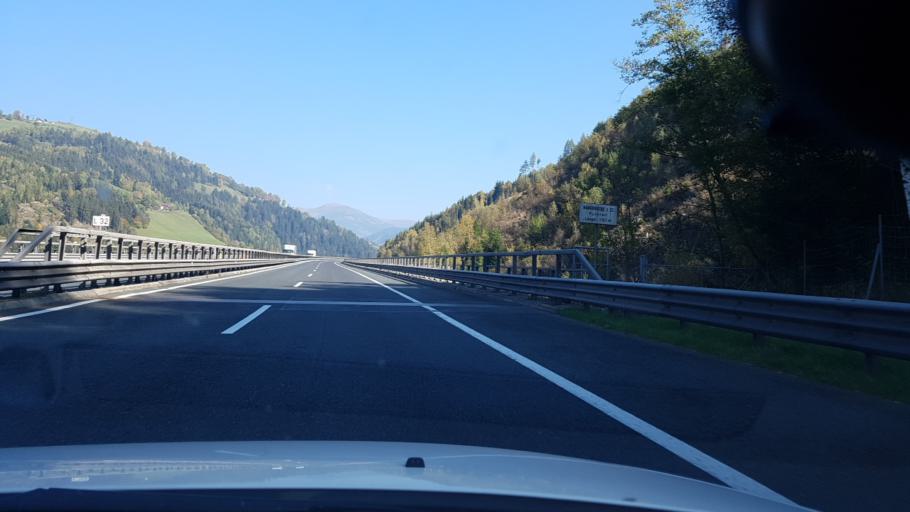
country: AT
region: Carinthia
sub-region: Politischer Bezirk Spittal an der Drau
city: Gmuend
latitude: 46.9128
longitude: 13.5580
